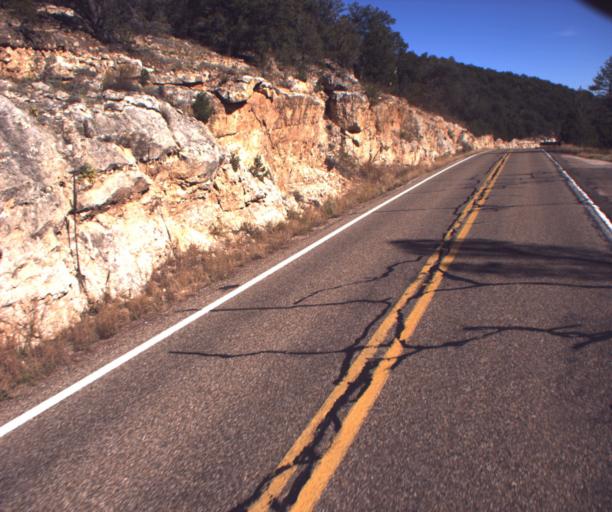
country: US
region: Arizona
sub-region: Coconino County
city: Fredonia
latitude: 36.7339
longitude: -112.1677
